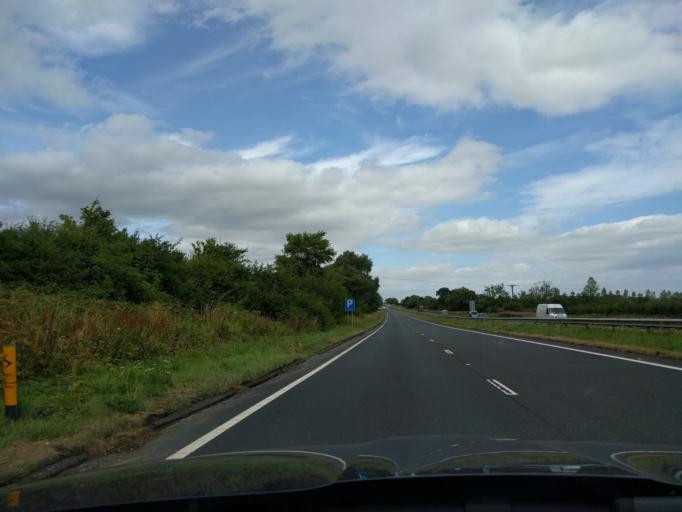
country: GB
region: England
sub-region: Northumberland
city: Felton
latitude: 55.3237
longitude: -1.7247
